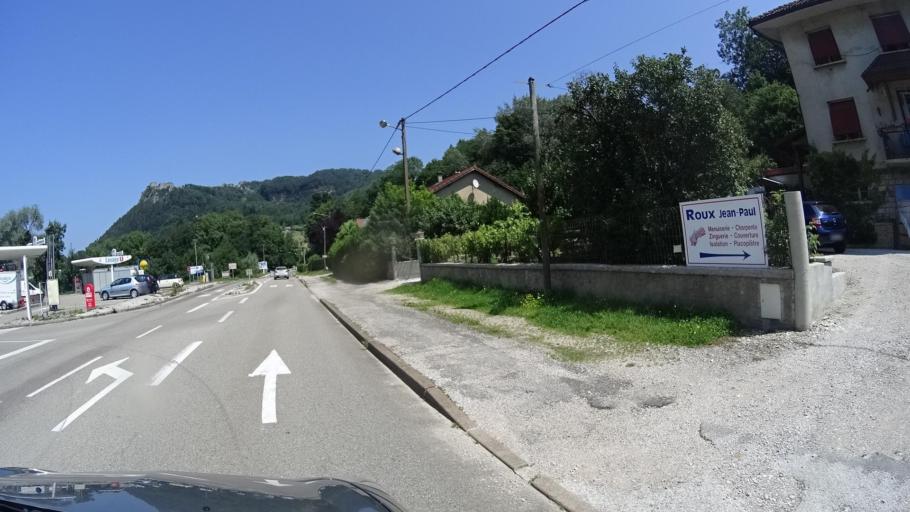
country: FR
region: Franche-Comte
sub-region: Departement du Jura
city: Salins-les-Bains
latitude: 46.9250
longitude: 5.8861
